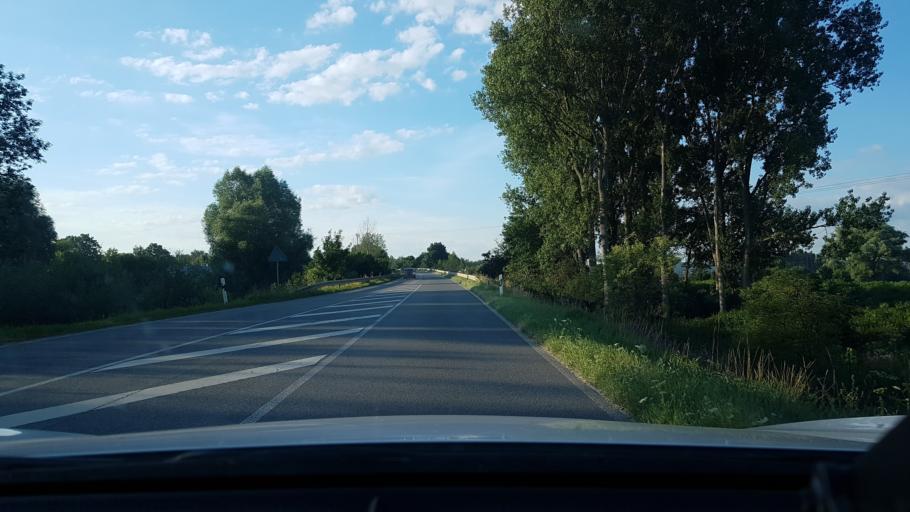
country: DE
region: Baden-Wuerttemberg
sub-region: Tuebingen Region
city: Warthausen
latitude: 48.1658
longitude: 9.8141
